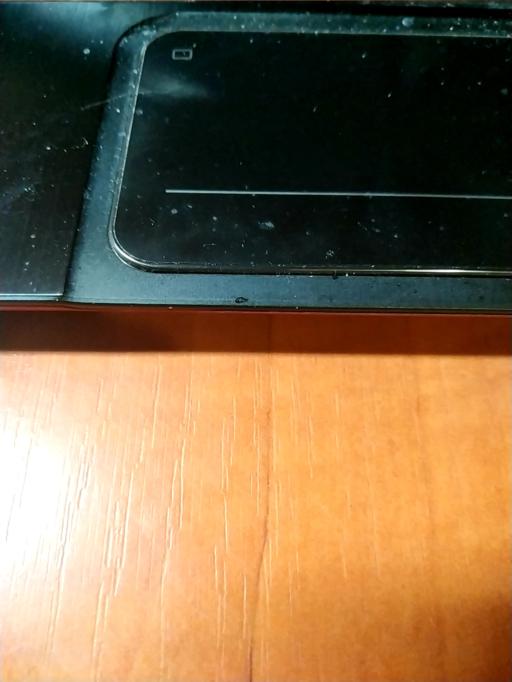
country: RU
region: Tverskaya
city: Ves'yegonsk
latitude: 58.7299
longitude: 37.5438
